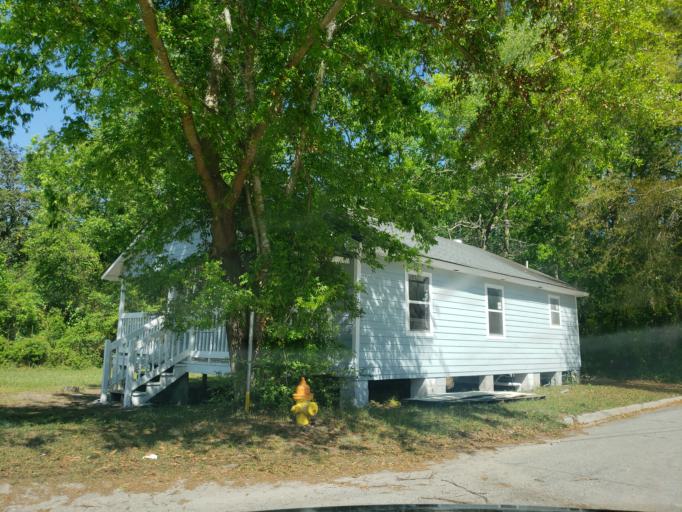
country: US
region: Georgia
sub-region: Chatham County
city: Thunderbolt
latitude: 32.0363
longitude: -81.0643
